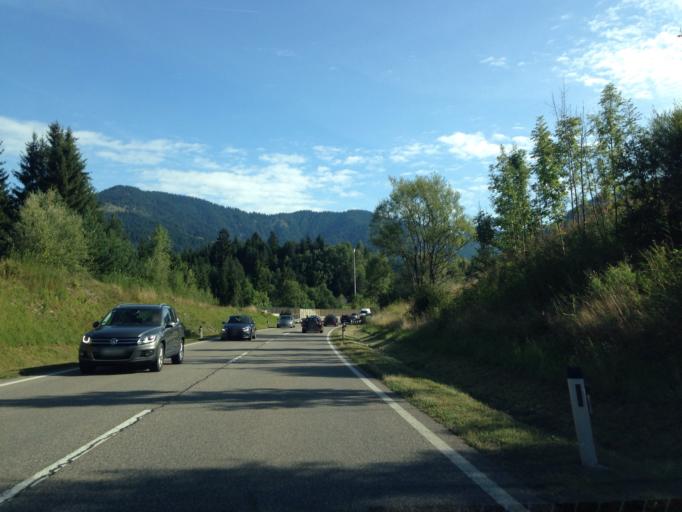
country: AT
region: Tyrol
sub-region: Politischer Bezirk Reutte
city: Breitenwang
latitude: 47.4841
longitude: 10.7386
